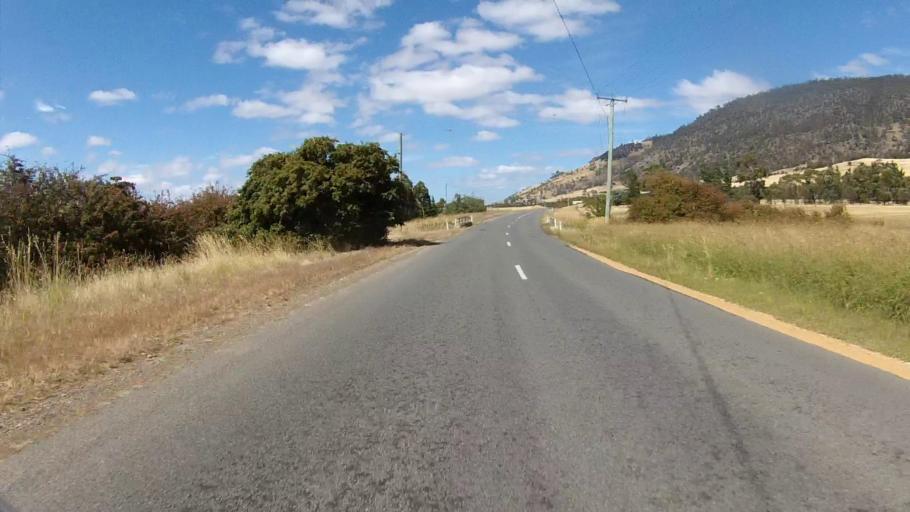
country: AU
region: Tasmania
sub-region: Sorell
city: Sorell
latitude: -42.6215
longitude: 147.4297
